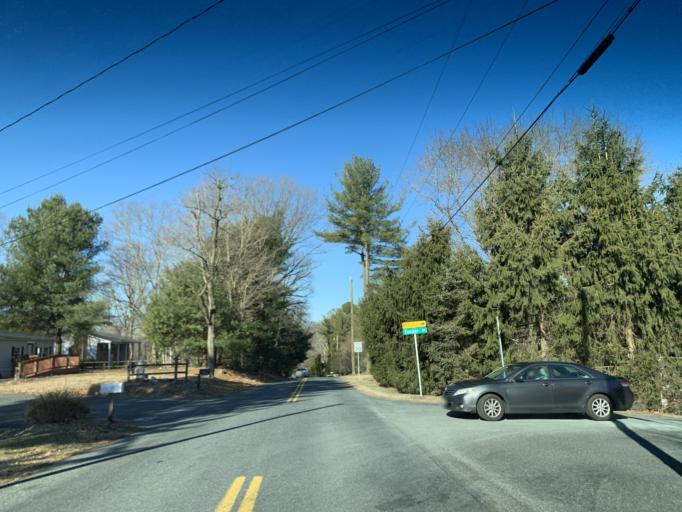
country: US
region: Maryland
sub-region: Harford County
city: South Bel Air
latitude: 39.6281
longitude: -76.2891
